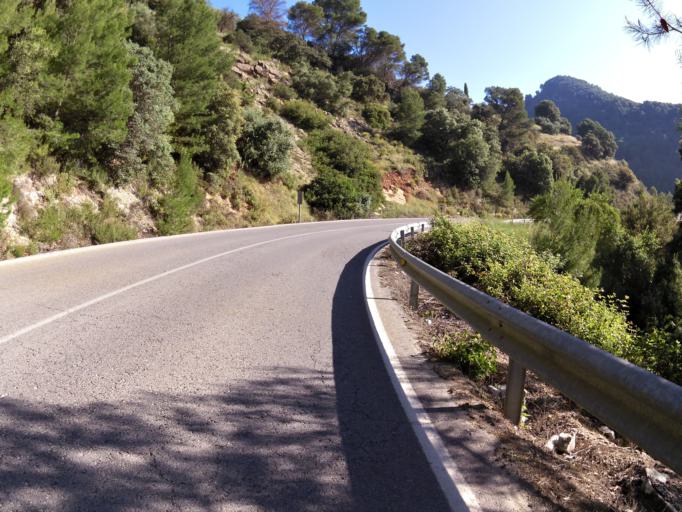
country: ES
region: Andalusia
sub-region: Provincia de Granada
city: Huetor-Tajar
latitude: 37.2727
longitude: -4.0752
